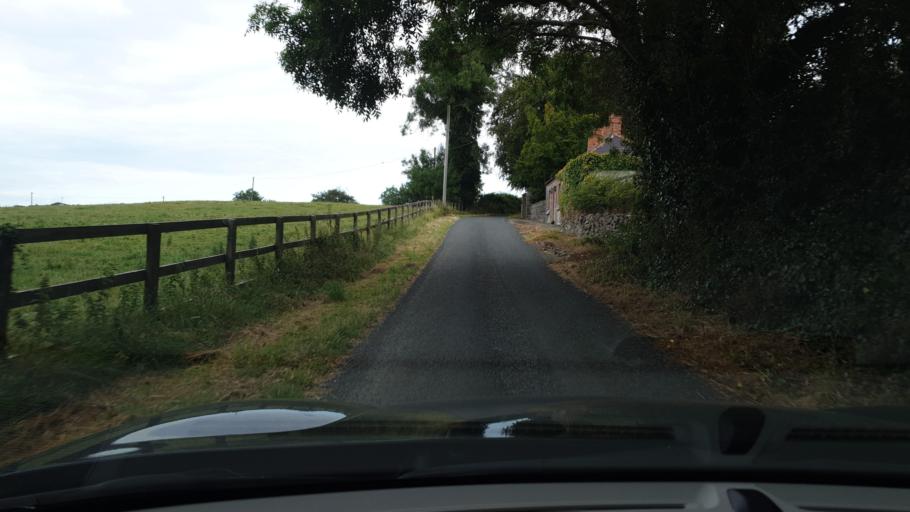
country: IE
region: Leinster
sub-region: An Mhi
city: Ashbourne
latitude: 53.5540
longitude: -6.3874
